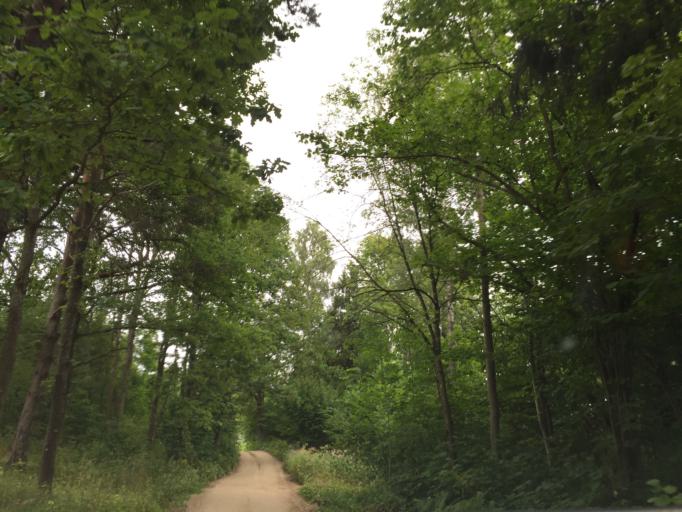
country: LV
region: Kegums
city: Kegums
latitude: 56.7500
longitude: 24.7106
